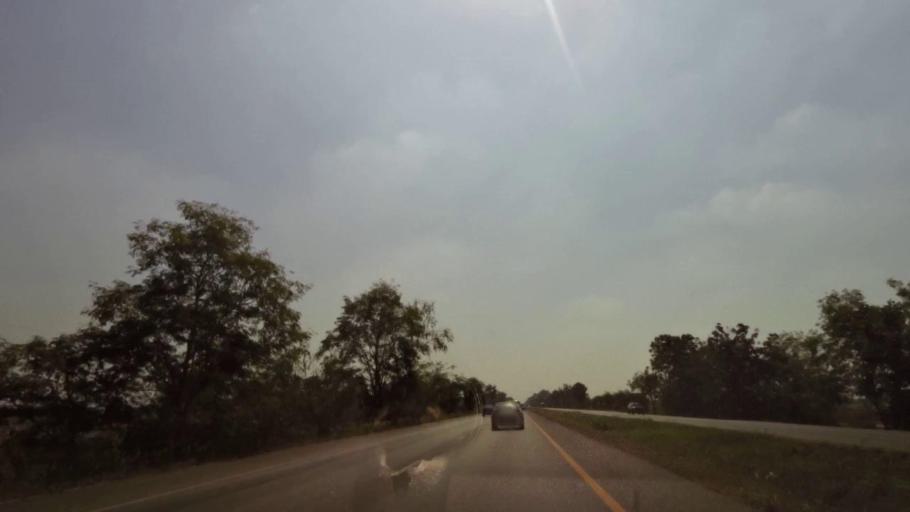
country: TH
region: Phichit
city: Wachira Barami
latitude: 16.4513
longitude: 100.1464
